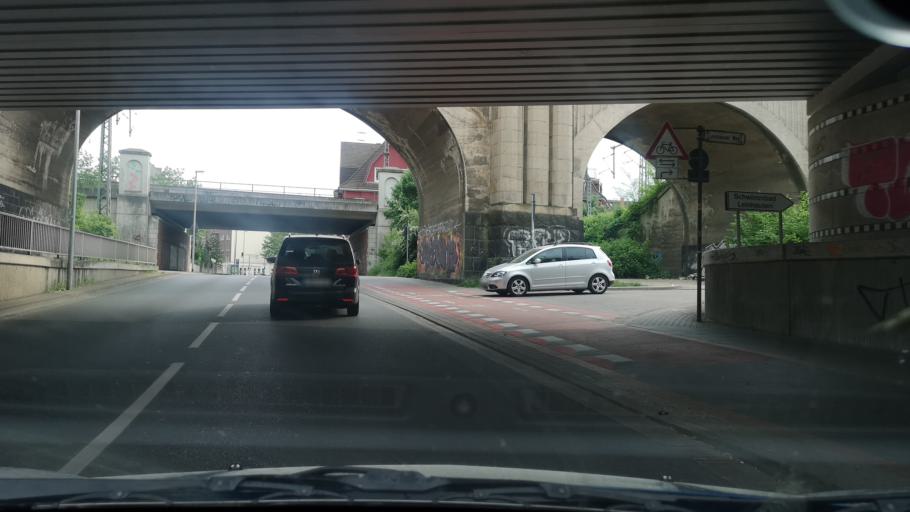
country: DE
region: Lower Saxony
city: Hannover
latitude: 52.3983
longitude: 9.6924
